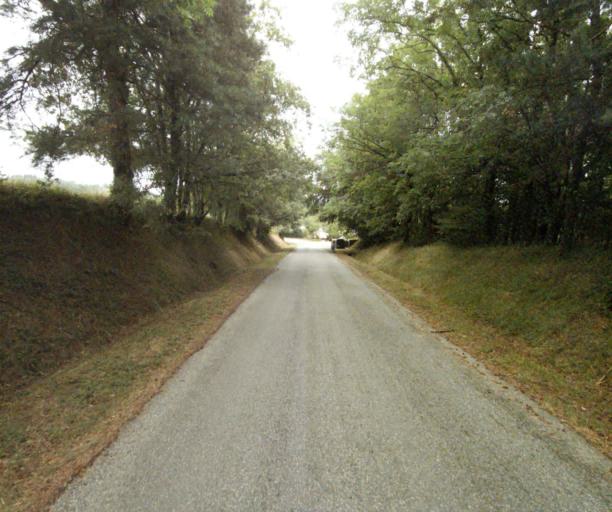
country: FR
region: Midi-Pyrenees
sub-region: Departement du Tarn
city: Soreze
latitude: 43.4072
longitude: 2.0862
